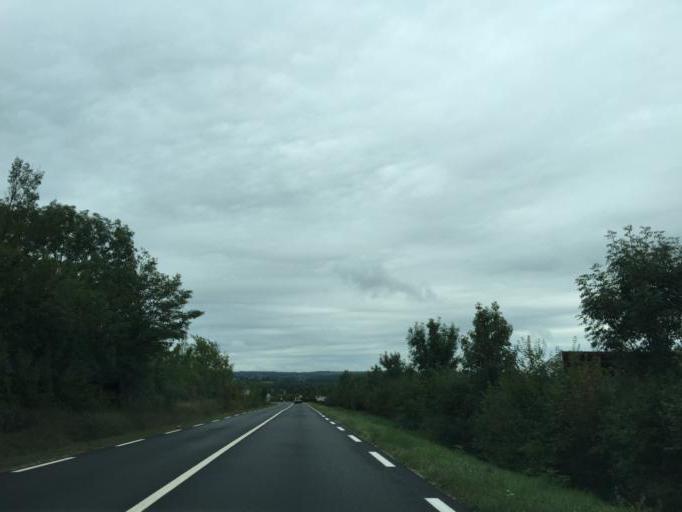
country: FR
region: Midi-Pyrenees
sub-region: Departement de l'Aveyron
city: Bozouls
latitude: 44.4783
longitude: 2.7326
